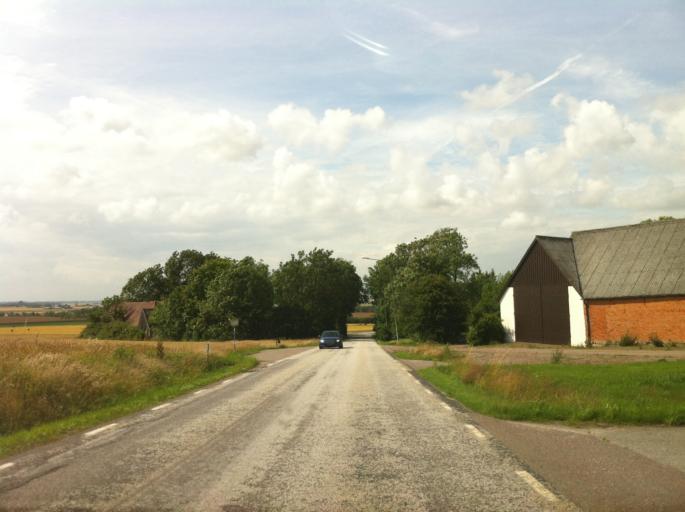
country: SE
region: Skane
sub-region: Lunds Kommun
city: Genarp
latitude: 55.5131
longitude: 13.4078
